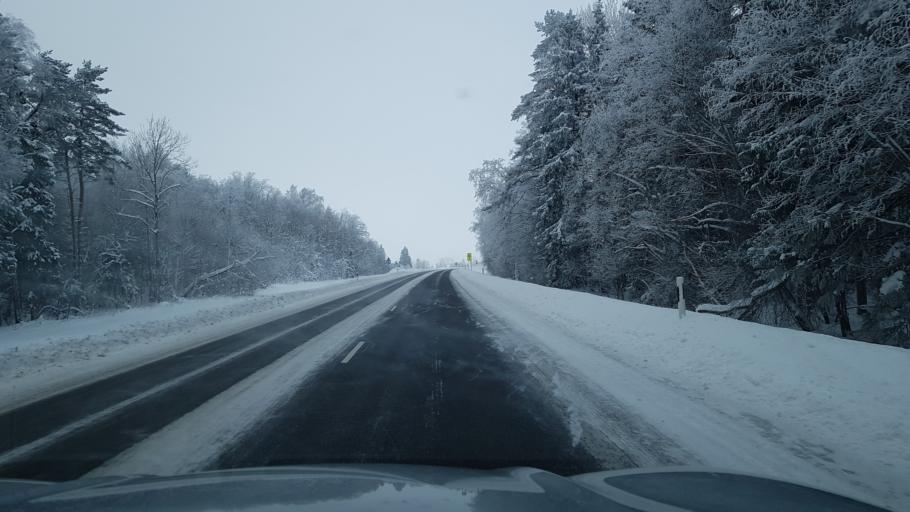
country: EE
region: Ida-Virumaa
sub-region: Johvi vald
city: Johvi
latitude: 59.3065
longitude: 27.3933
